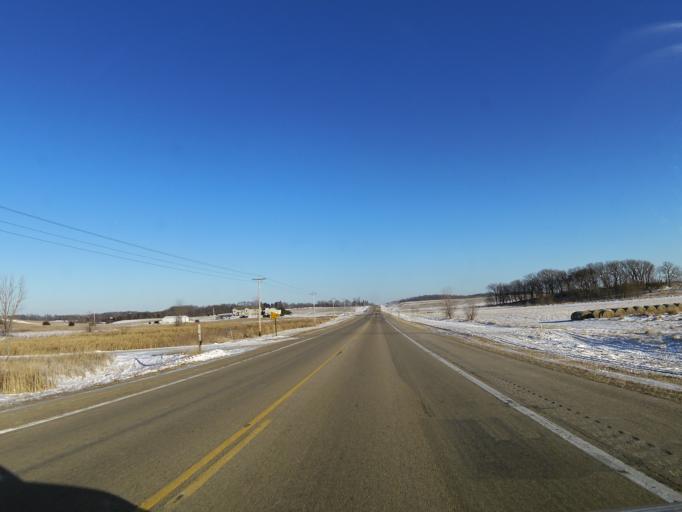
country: US
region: Minnesota
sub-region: Rice County
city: Lonsdale
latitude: 44.4862
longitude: -93.4772
